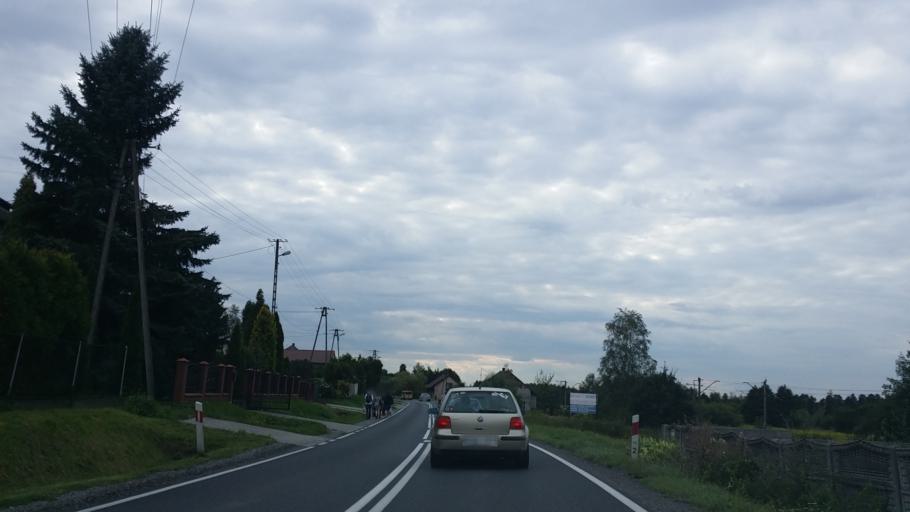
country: PL
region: Lesser Poland Voivodeship
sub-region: Powiat krakowski
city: Czernichow
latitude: 49.9611
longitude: 19.6839
